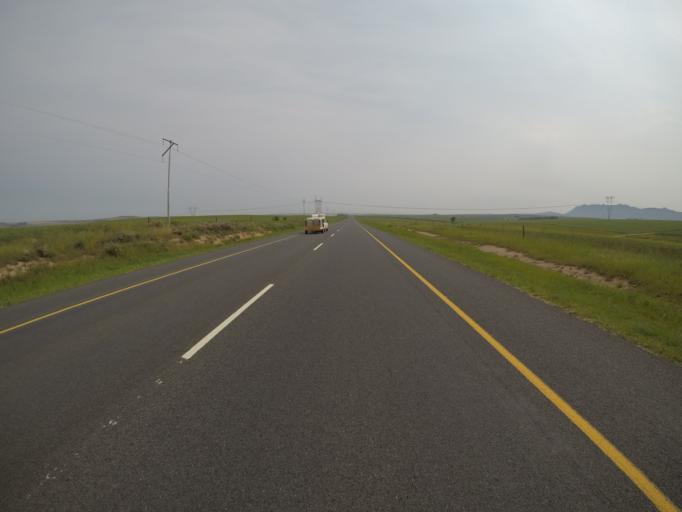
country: ZA
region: Western Cape
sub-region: West Coast District Municipality
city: Malmesbury
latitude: -33.4954
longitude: 18.8289
